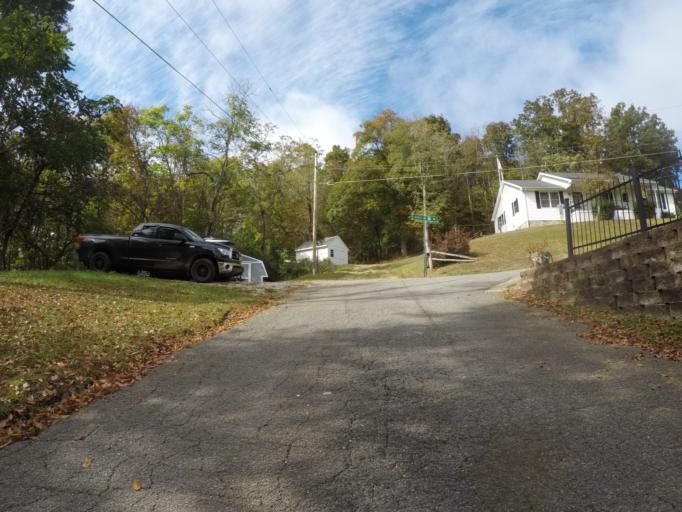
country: US
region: West Virginia
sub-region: Cabell County
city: Huntington
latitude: 38.3959
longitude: -82.3909
